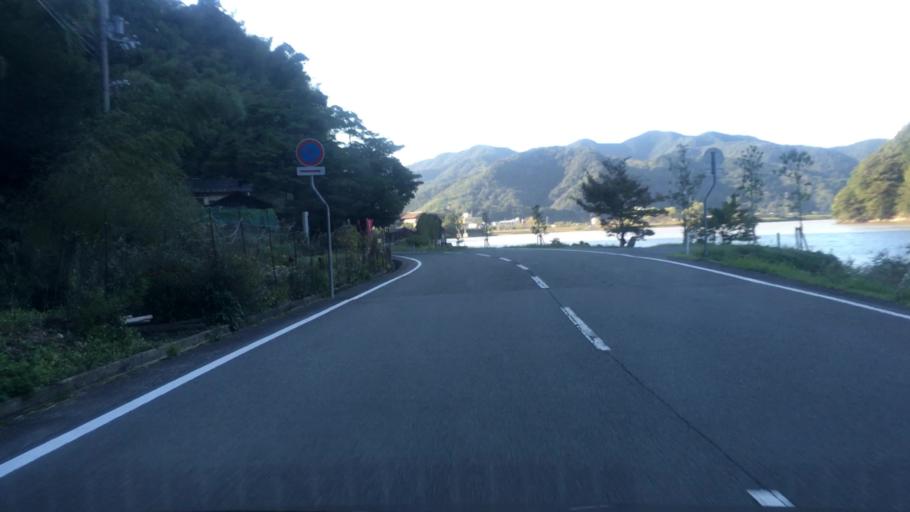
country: JP
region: Hyogo
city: Toyooka
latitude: 35.6165
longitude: 134.8239
